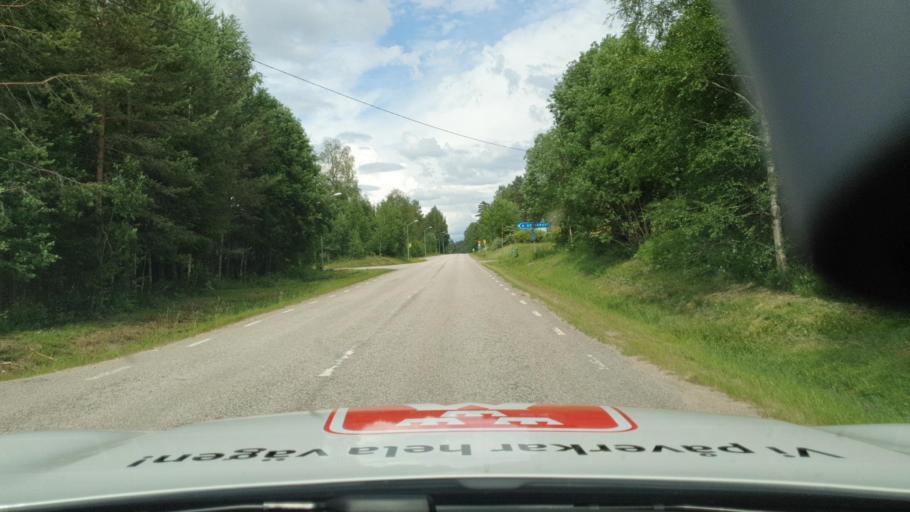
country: NO
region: Hedmark
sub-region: Trysil
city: Innbygda
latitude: 60.9600
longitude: 12.4724
